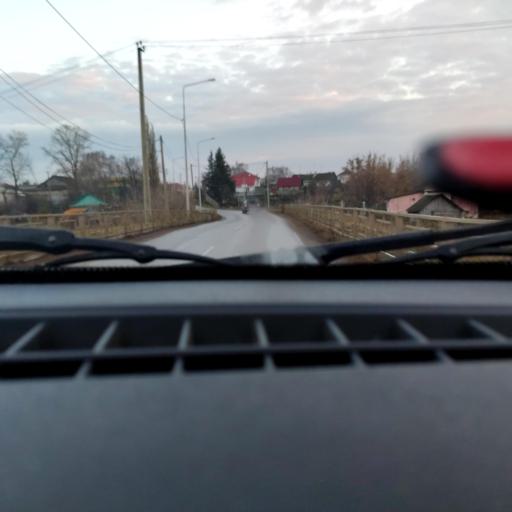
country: RU
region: Bashkortostan
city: Avdon
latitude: 54.5002
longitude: 55.8824
